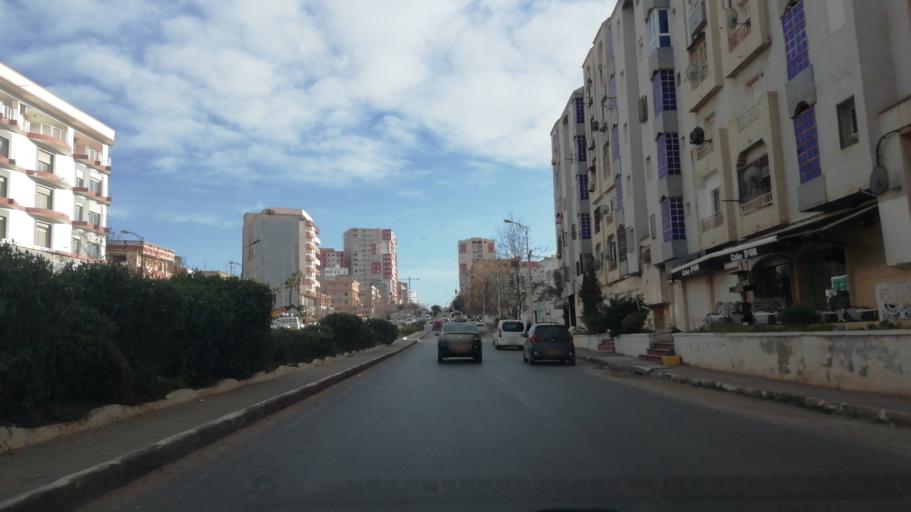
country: DZ
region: Oran
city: Bir el Djir
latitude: 35.7275
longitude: -0.5856
